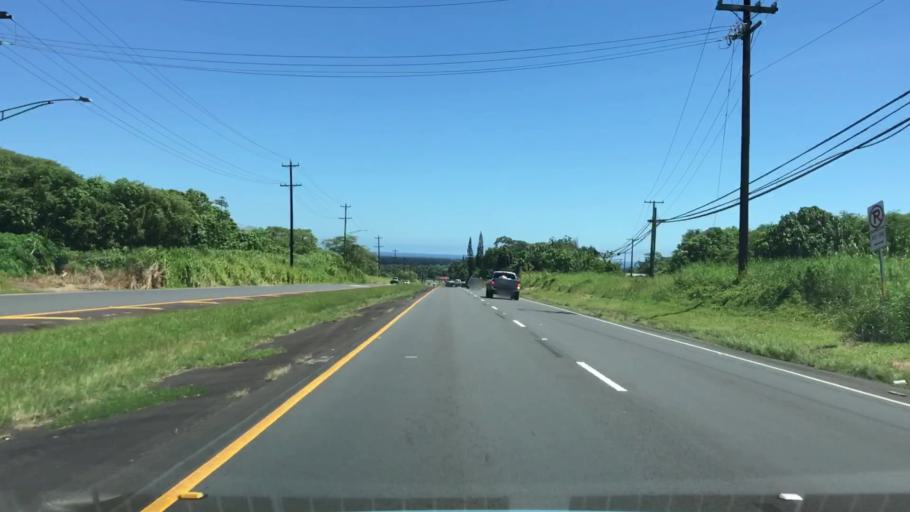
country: US
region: Hawaii
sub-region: Hawaii County
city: Kea'au
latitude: 19.6155
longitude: -155.0459
